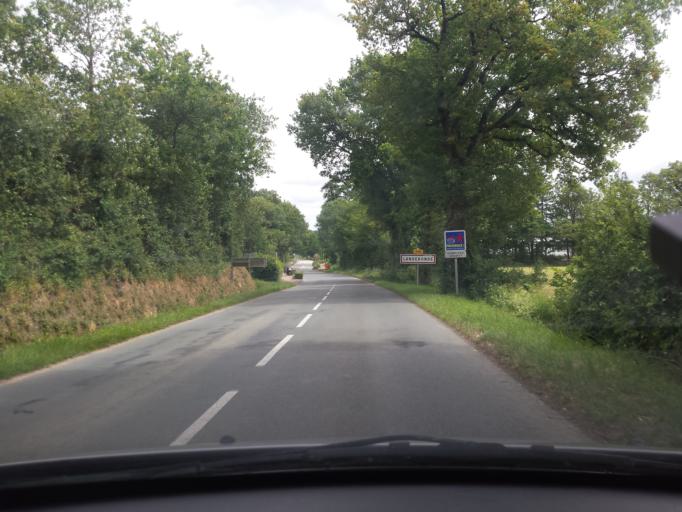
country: FR
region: Pays de la Loire
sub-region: Departement de la Vendee
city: Landeronde
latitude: 46.6608
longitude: -1.5805
